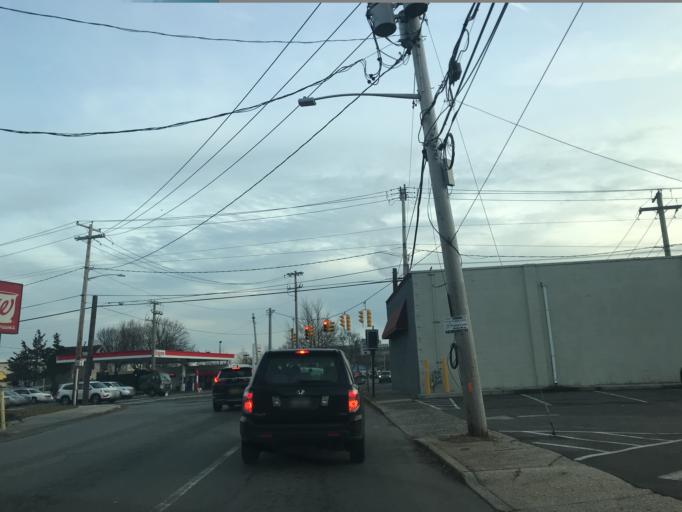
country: US
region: New York
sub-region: Nassau County
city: Westbury
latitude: 40.7477
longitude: -73.5931
